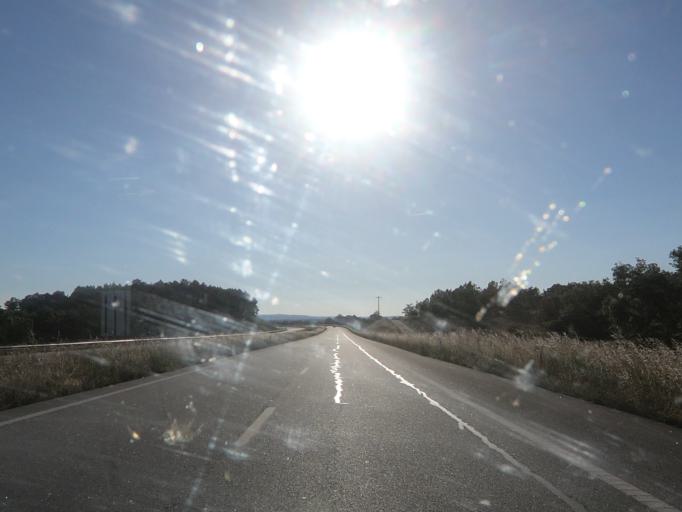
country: PT
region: Guarda
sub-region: Pinhel
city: Pinhel
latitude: 40.6098
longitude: -6.9981
